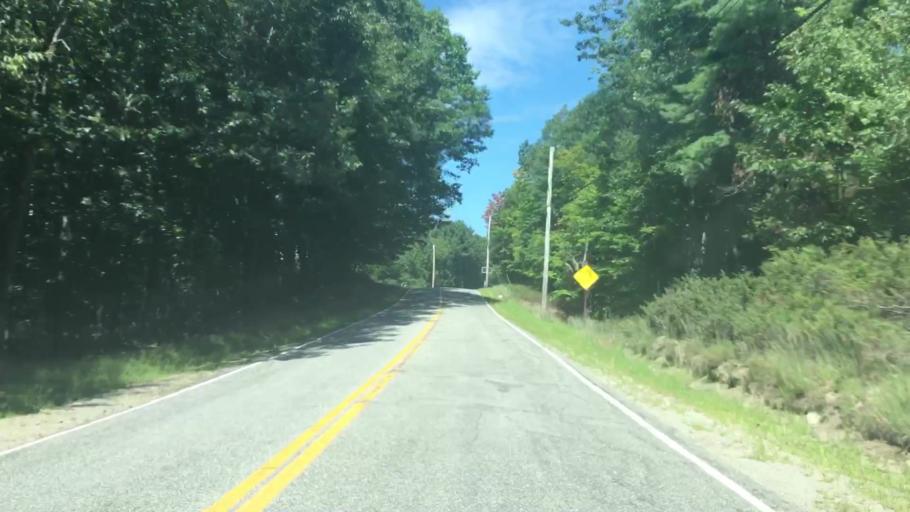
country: US
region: Maine
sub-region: Kennebec County
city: Monmouth
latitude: 44.1582
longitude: -69.9446
